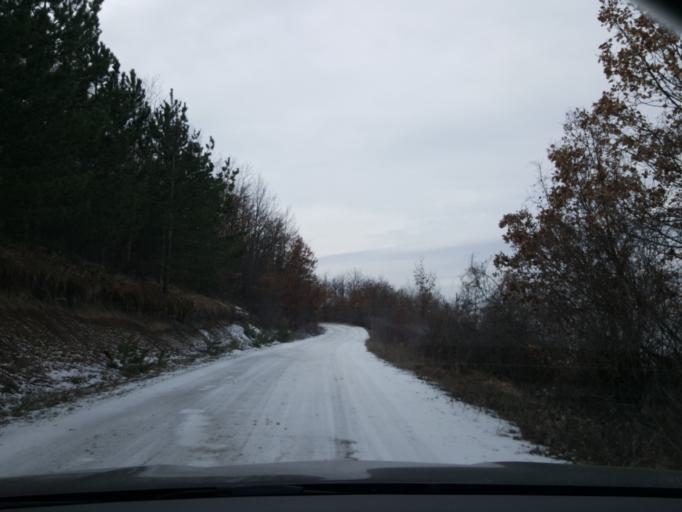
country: RS
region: Central Serbia
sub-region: Pirotski Okrug
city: Dimitrovgrad
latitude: 43.0003
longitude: 22.7486
